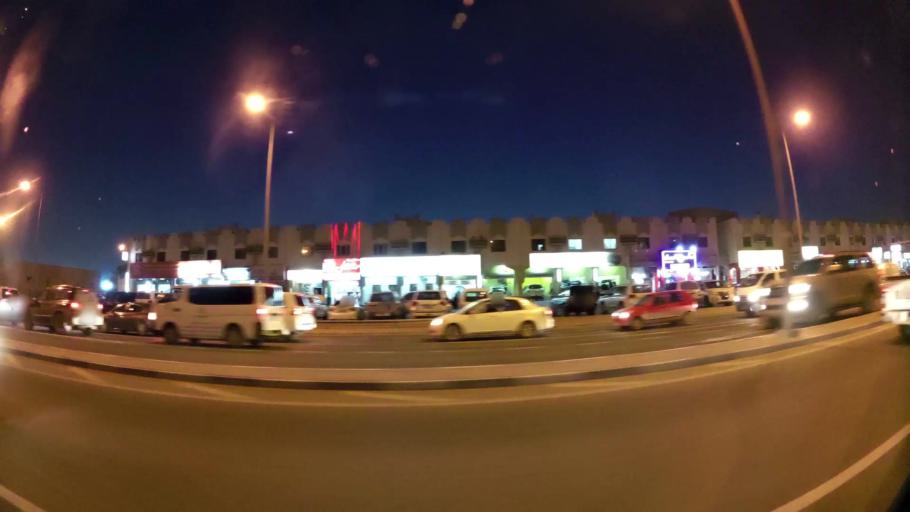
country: QA
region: Baladiyat ar Rayyan
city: Ar Rayyan
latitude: 25.2866
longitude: 51.4312
